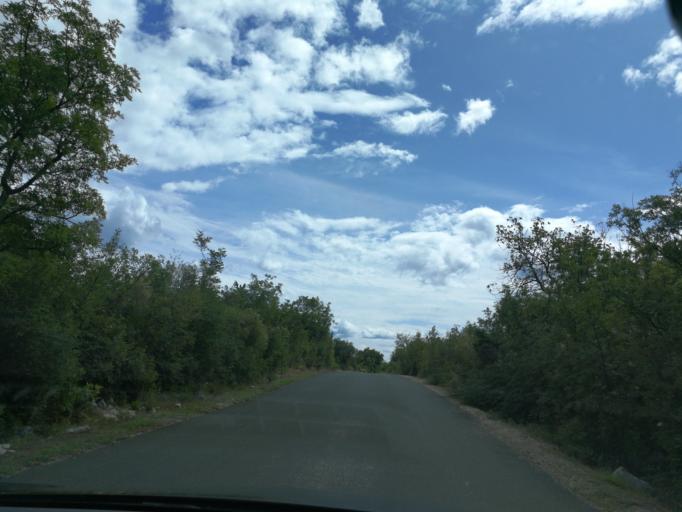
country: HR
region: Primorsko-Goranska
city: Omisalj
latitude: 45.2018
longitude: 14.5714
